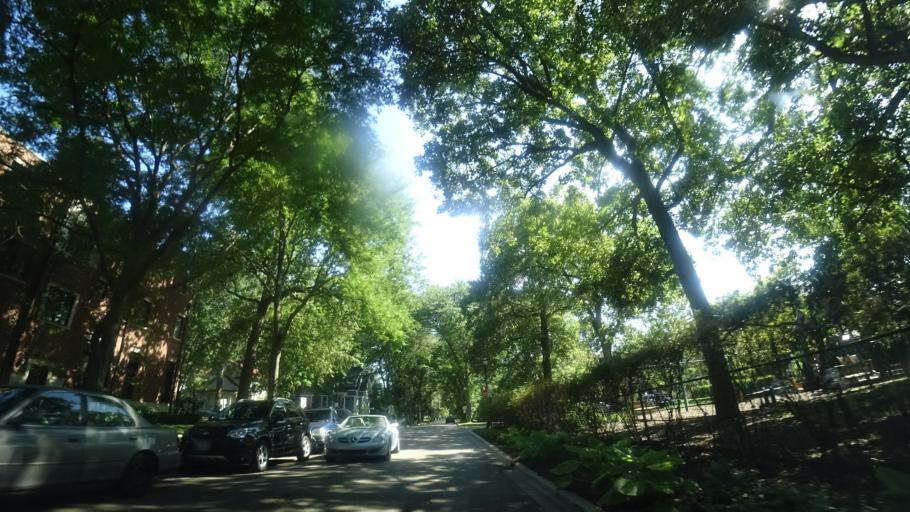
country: US
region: Illinois
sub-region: Cook County
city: Wilmette
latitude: 42.0637
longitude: -87.7034
